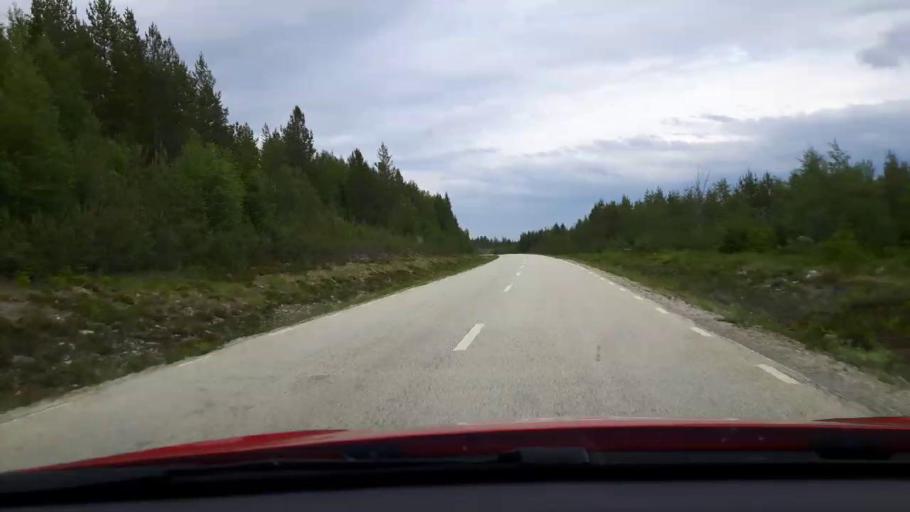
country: SE
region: Jaemtland
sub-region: Bergs Kommun
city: Hoverberg
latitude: 62.7057
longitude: 13.9420
